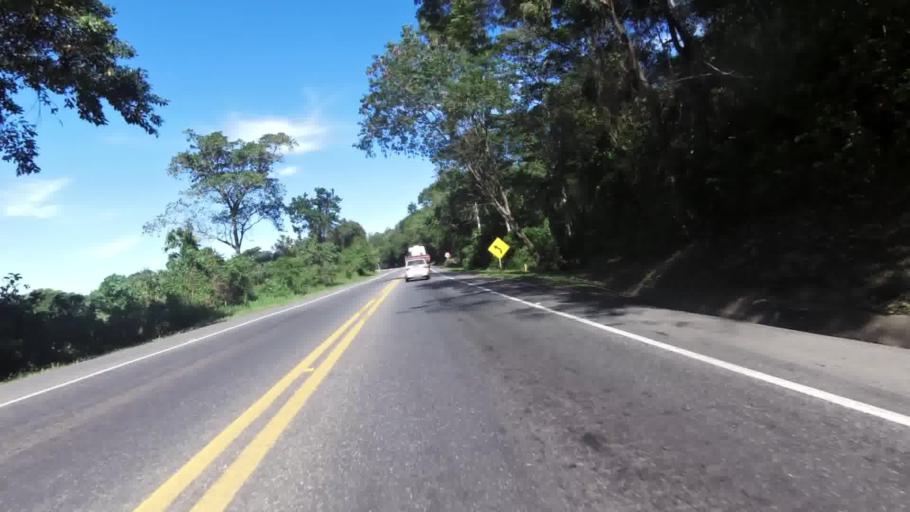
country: BR
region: Espirito Santo
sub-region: Iconha
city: Iconha
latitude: -20.8107
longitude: -40.8376
